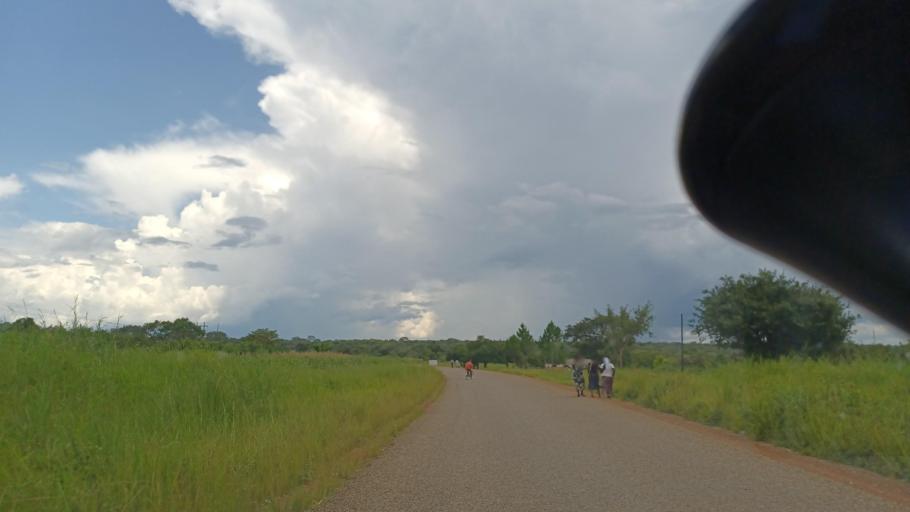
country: ZM
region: North-Western
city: Kasempa
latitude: -12.8632
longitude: 26.0377
